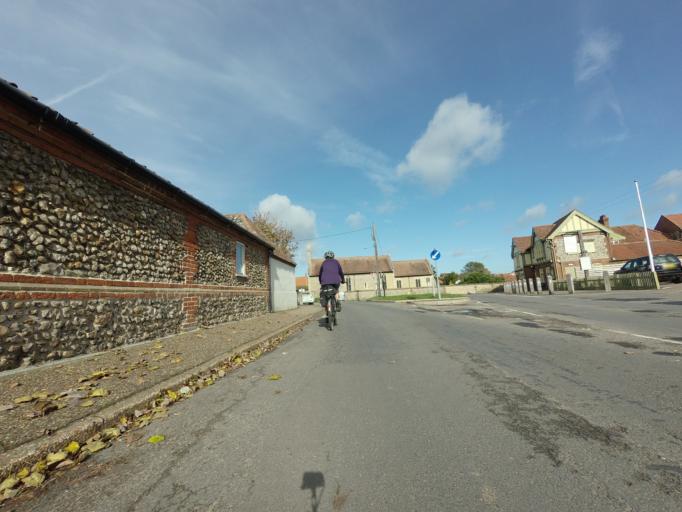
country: GB
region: England
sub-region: Norfolk
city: Wells-next-the-Sea
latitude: 52.9456
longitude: 0.7306
